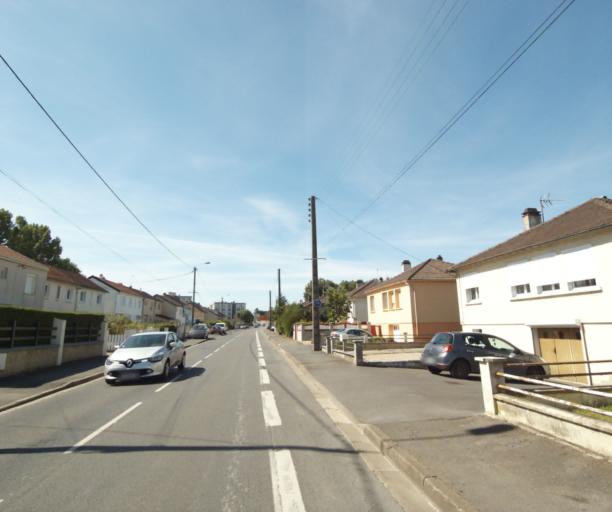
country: FR
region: Champagne-Ardenne
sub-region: Departement des Ardennes
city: Charleville-Mezieres
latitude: 49.7517
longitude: 4.7155
